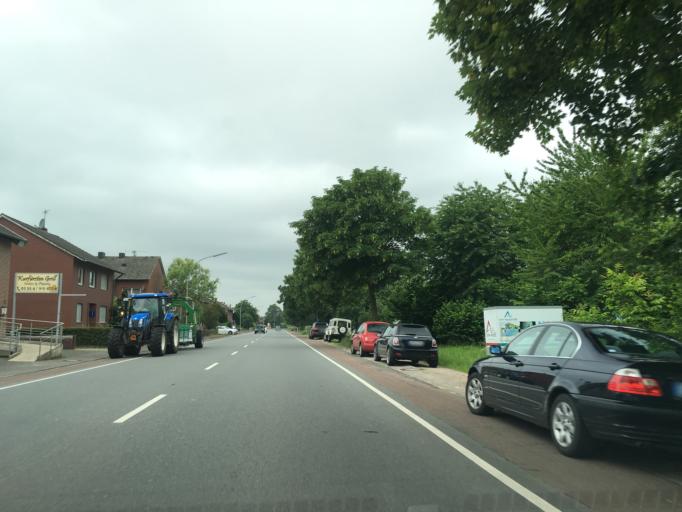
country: DE
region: North Rhine-Westphalia
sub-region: Regierungsbezirk Munster
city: Laer
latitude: 52.0587
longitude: 7.3601
